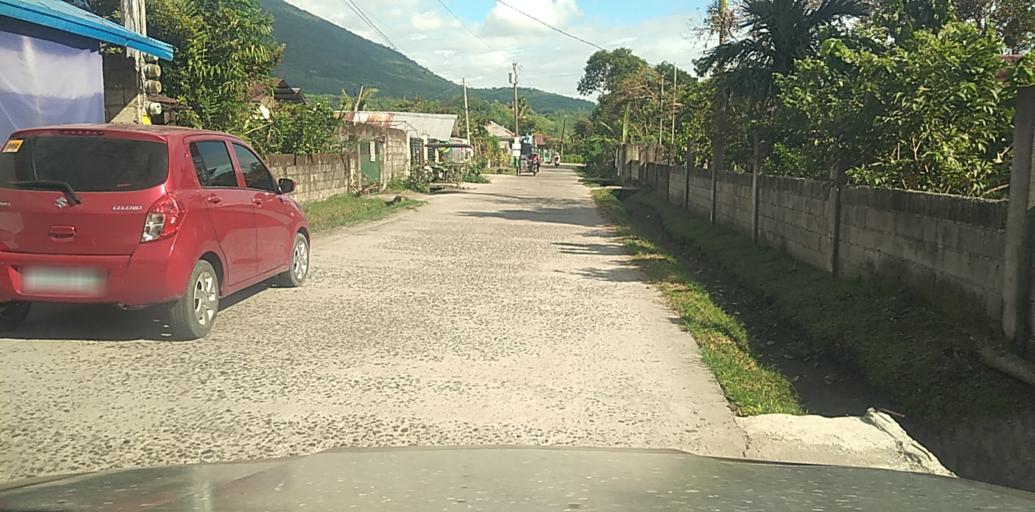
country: PH
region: Central Luzon
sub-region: Province of Pampanga
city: Panlinlang
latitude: 15.1909
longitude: 120.6896
